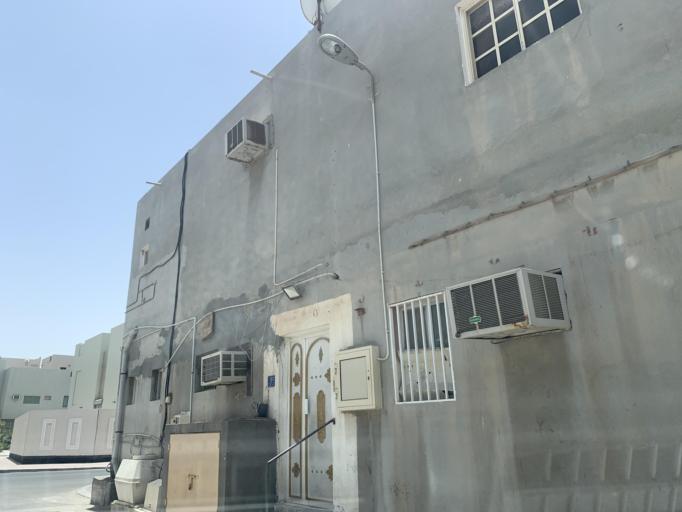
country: BH
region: Northern
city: Sitrah
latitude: 26.1613
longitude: 50.6236
